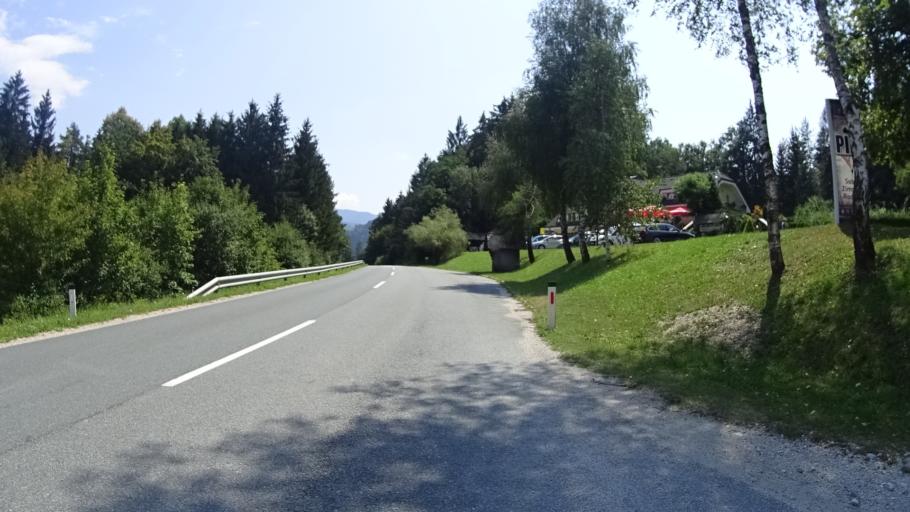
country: SI
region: Mezica
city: Mezica
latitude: 46.5601
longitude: 14.8486
